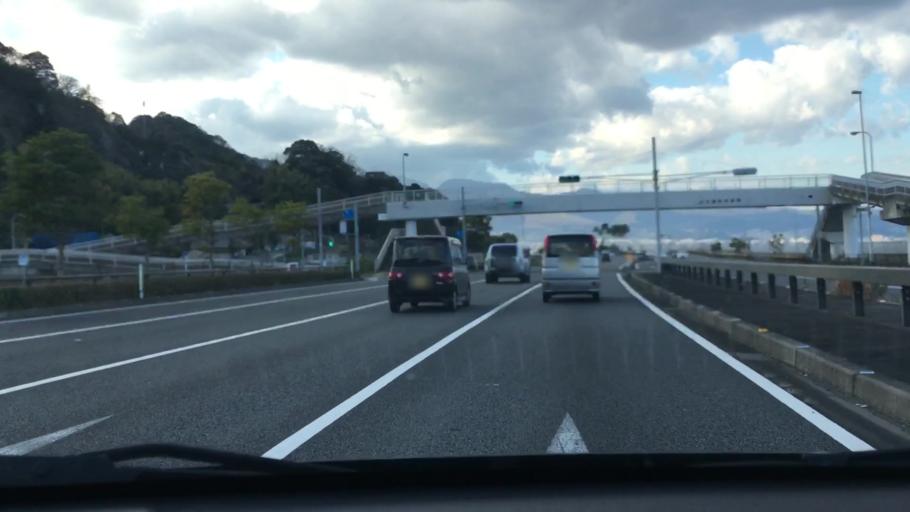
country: JP
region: Oita
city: Oita
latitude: 33.2532
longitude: 131.5646
